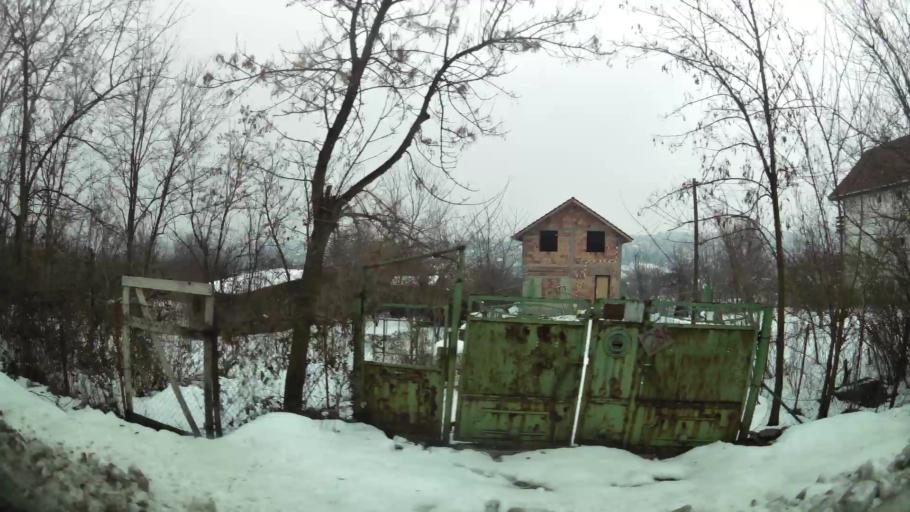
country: RS
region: Central Serbia
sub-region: Belgrade
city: Zvezdara
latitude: 44.7587
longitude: 20.5201
